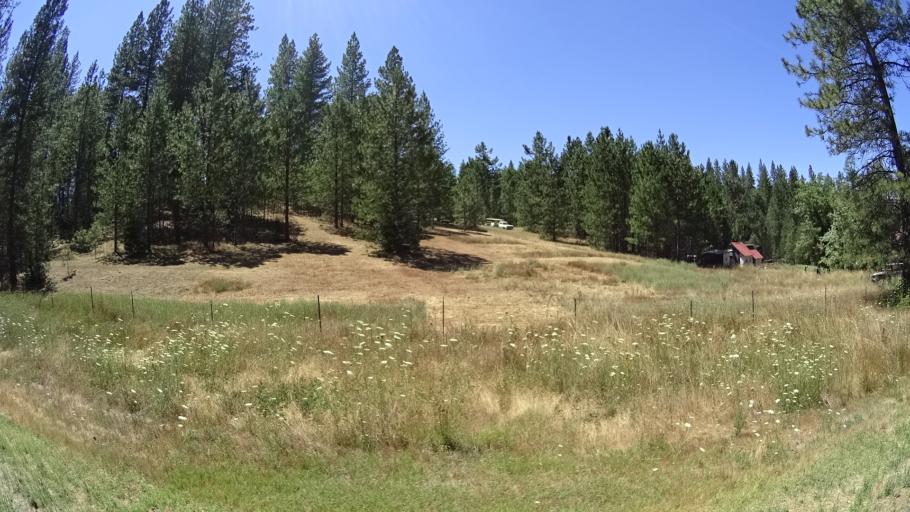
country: US
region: California
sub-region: Calaveras County
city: Mountain Ranch
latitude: 38.3218
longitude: -120.5204
